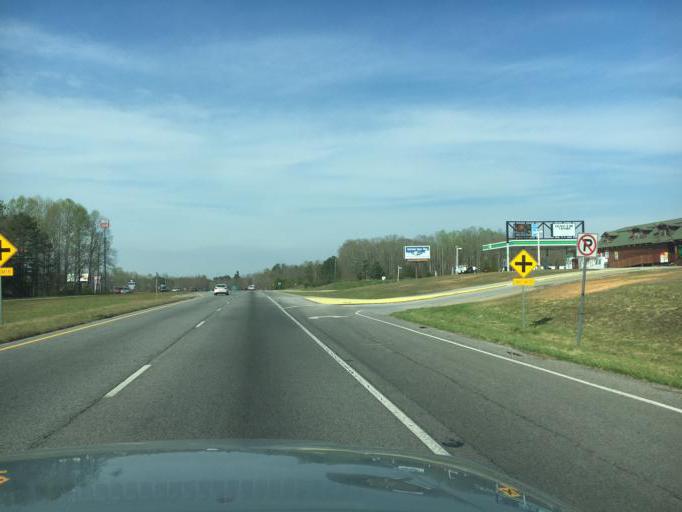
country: US
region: Georgia
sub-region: Banks County
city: Alto
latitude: 34.4849
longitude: -83.5837
